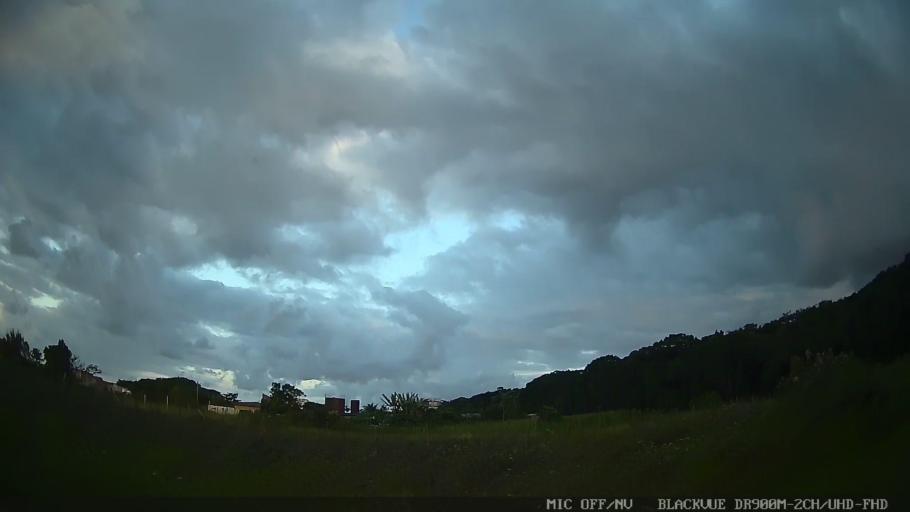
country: BR
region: Sao Paulo
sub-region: Itanhaem
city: Itanhaem
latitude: -24.1860
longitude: -46.8379
